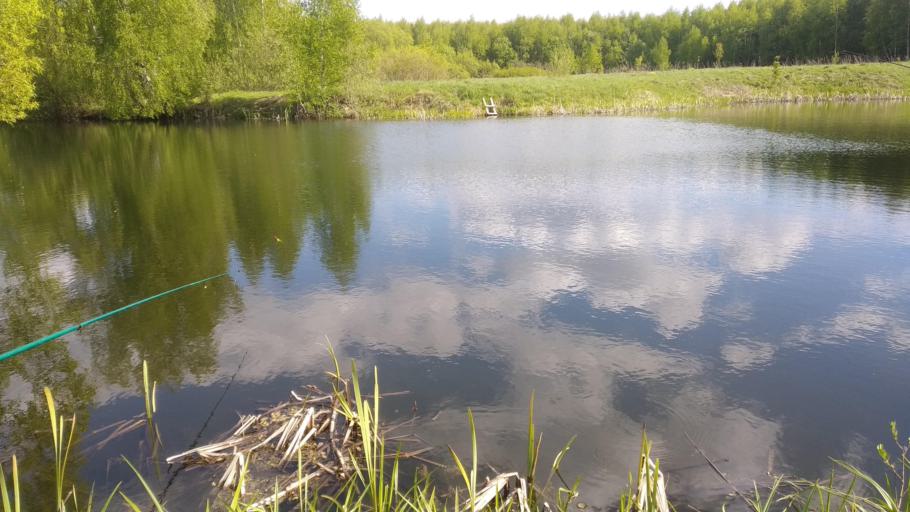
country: RU
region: Moskovskaya
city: Sychevo
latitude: 55.0412
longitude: 38.7068
